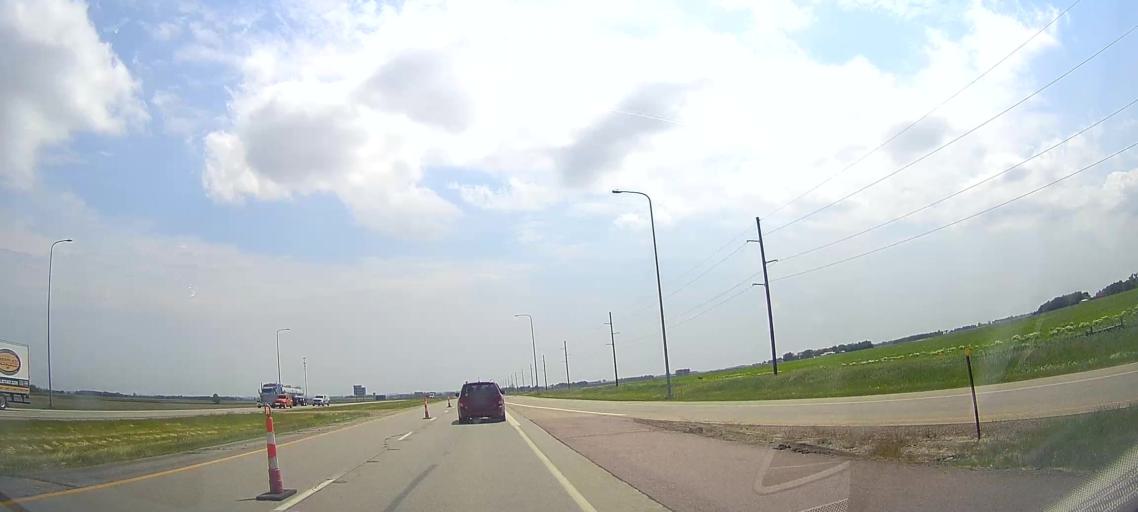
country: US
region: South Dakota
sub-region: Lincoln County
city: Lennox
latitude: 43.2975
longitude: -96.7964
